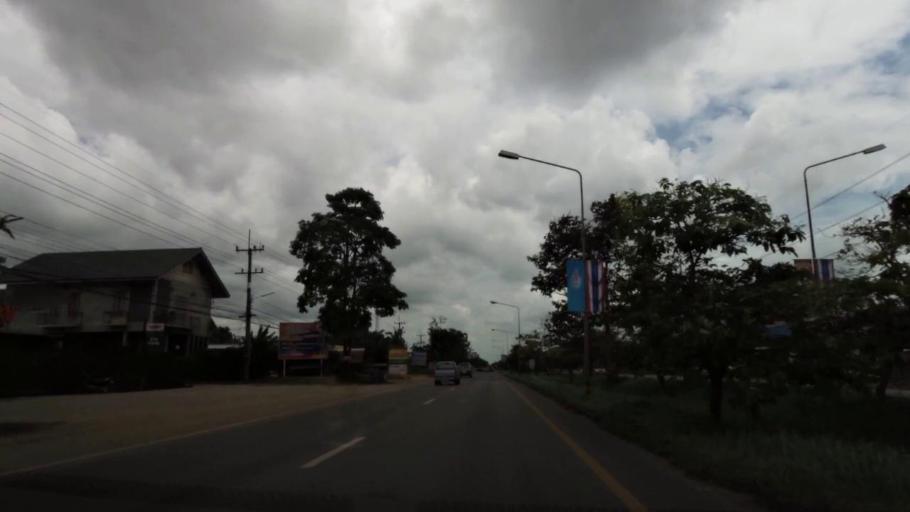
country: TH
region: Rayong
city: Klaeng
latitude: 12.7809
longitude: 101.6967
